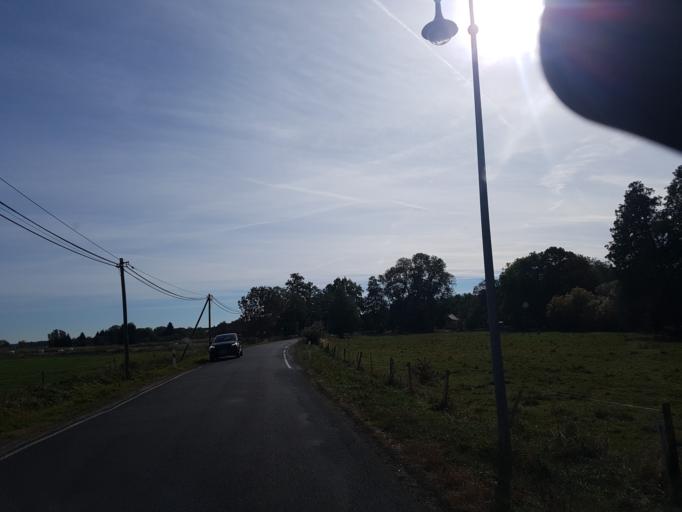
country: DE
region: Brandenburg
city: Schlieben
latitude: 51.7058
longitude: 13.4098
